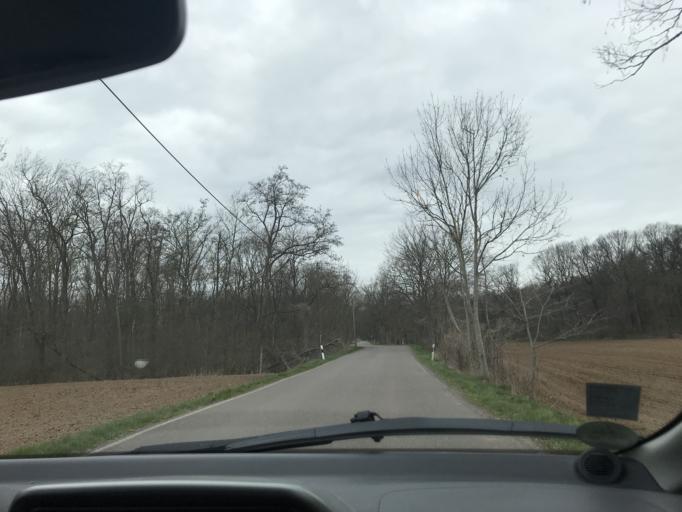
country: DE
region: Saxony
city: Schkeuditz
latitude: 51.3651
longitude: 12.2623
